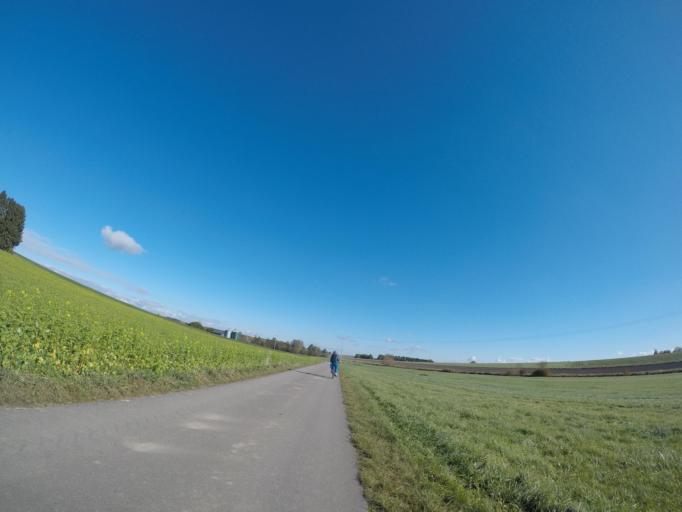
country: DE
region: Baden-Wuerttemberg
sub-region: Tuebingen Region
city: Durnau
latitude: 48.0650
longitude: 9.5569
